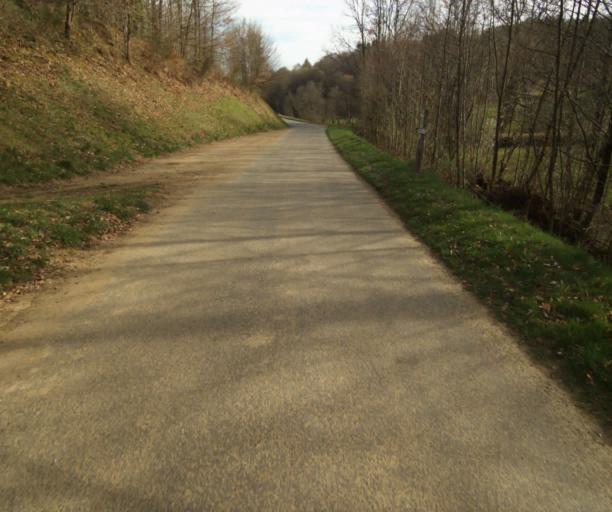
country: FR
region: Limousin
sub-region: Departement de la Correze
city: Naves
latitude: 45.2980
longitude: 1.7550
